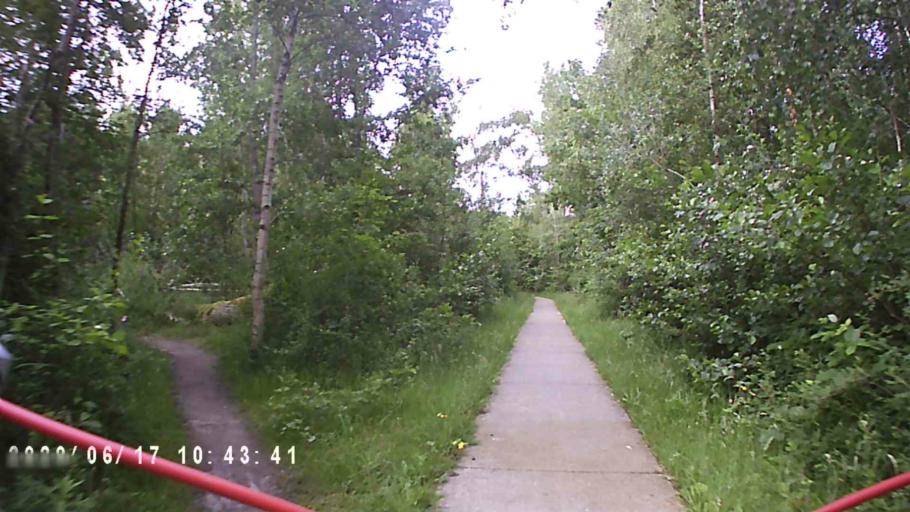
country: NL
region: Friesland
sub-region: Gemeente Dongeradeel
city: Anjum
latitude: 53.4060
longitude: 6.2269
